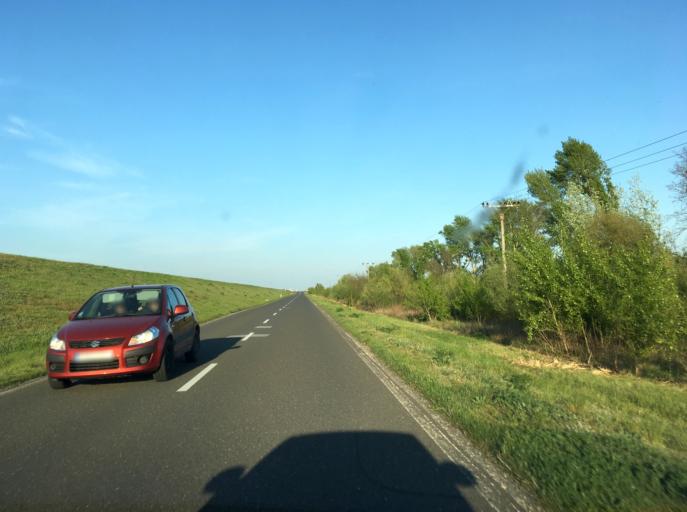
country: SK
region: Trnavsky
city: Samorin
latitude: 47.9970
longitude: 17.2934
